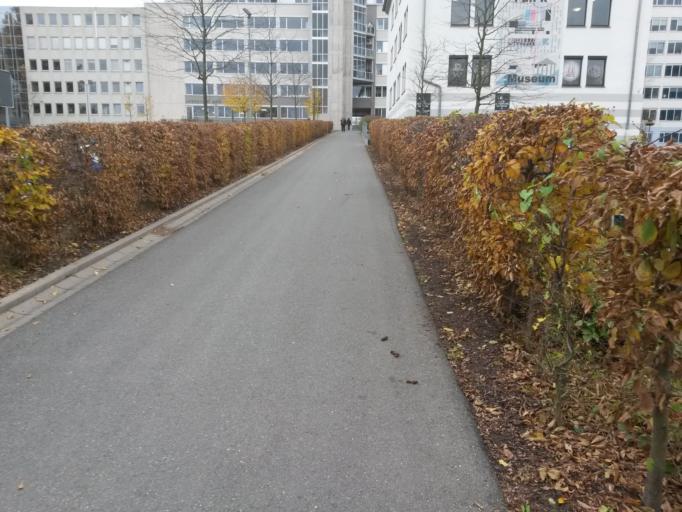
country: DE
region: Bavaria
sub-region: Regierungsbezirk Mittelfranken
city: Furth
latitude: 49.4691
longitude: 11.0125
